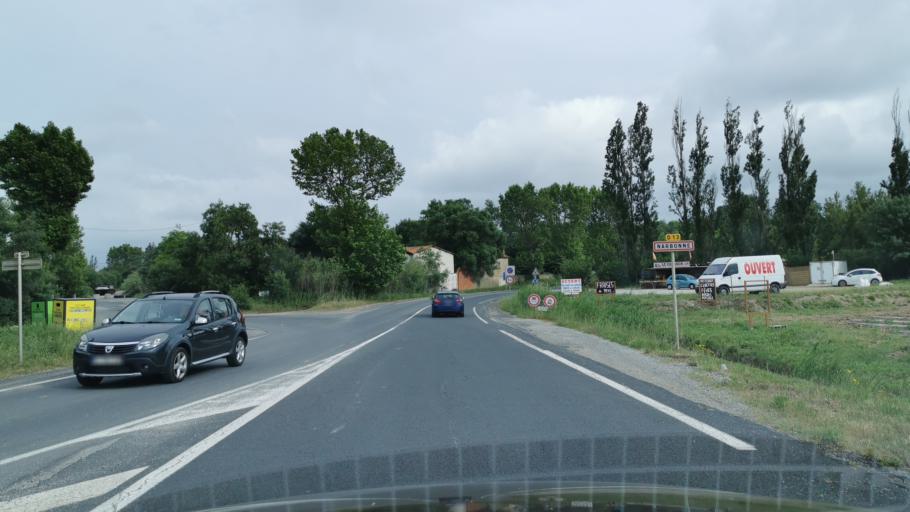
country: FR
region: Languedoc-Roussillon
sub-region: Departement de l'Aude
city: Narbonne
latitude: 43.1999
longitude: 3.0126
